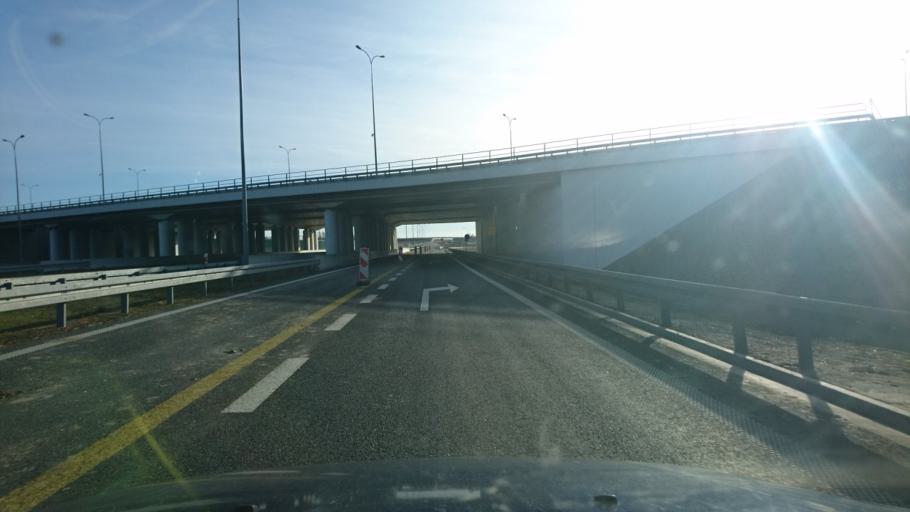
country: PL
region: Greater Poland Voivodeship
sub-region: Powiat kepinski
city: Kepno
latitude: 51.3164
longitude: 18.0085
